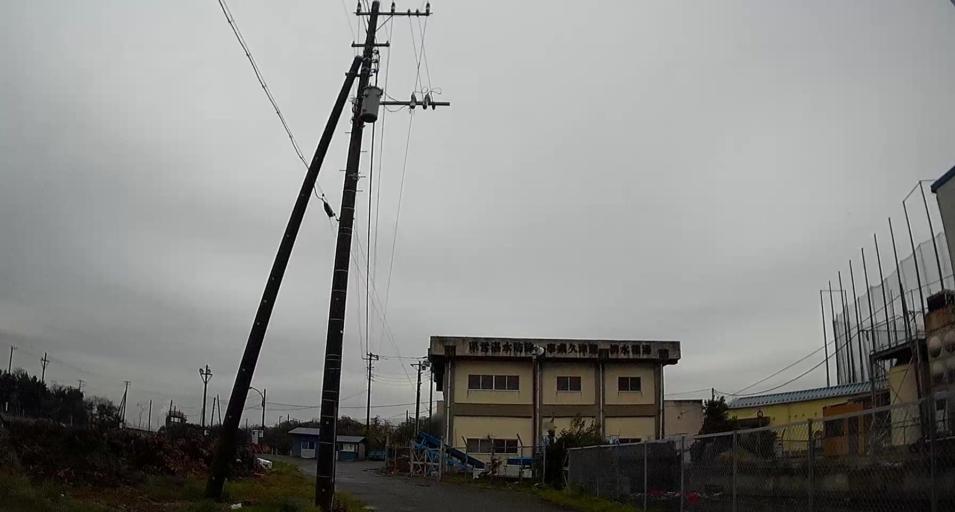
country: JP
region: Chiba
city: Kisarazu
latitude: 35.4056
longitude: 139.9035
